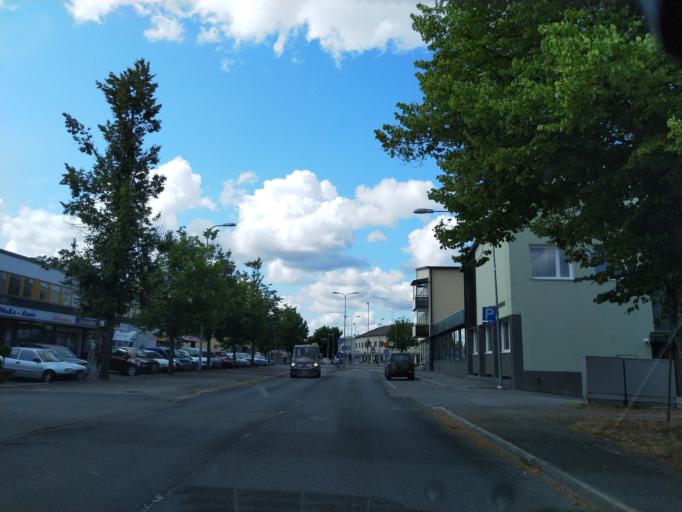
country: FI
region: Satakunta
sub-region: Pori
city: Huittinen
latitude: 61.1766
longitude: 22.6996
